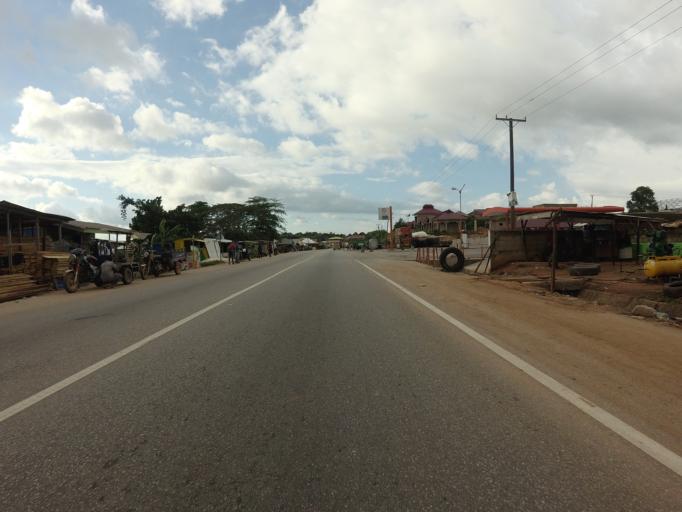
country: GH
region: Ashanti
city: Tafo
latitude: 6.8393
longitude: -1.6504
